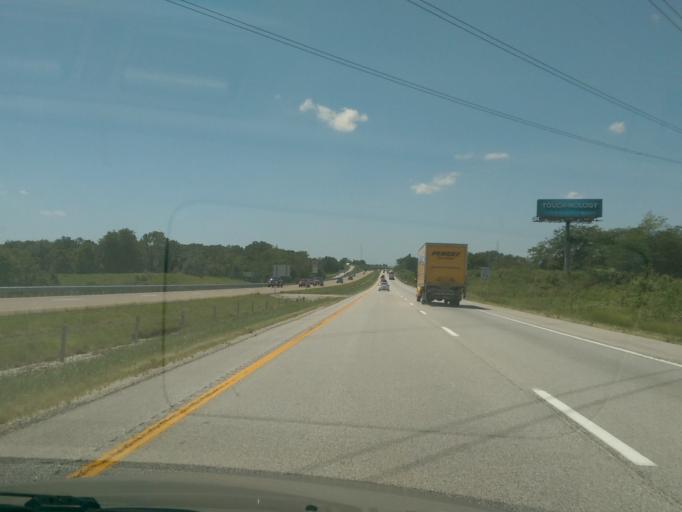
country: US
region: Missouri
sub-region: Cooper County
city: Boonville
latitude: 38.9356
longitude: -92.7878
